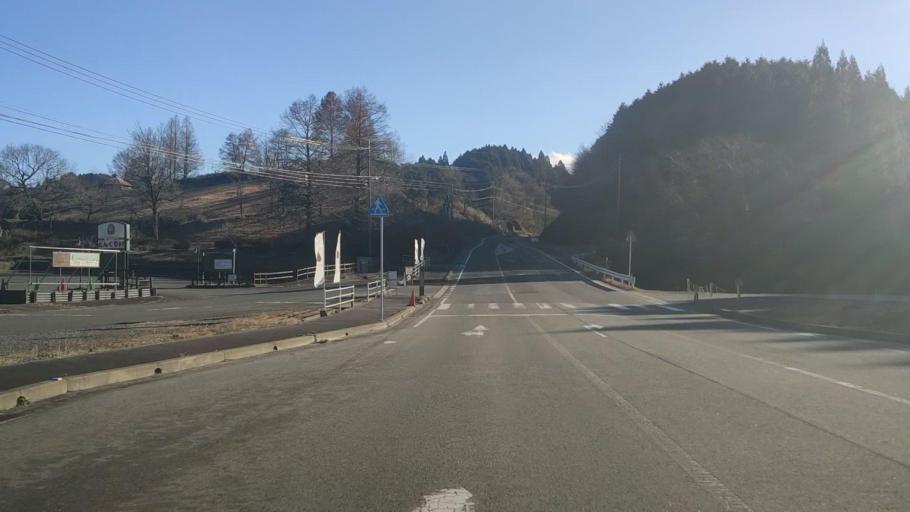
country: JP
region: Saga Prefecture
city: Kanzakimachi-kanzaki
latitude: 33.4063
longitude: 130.2724
